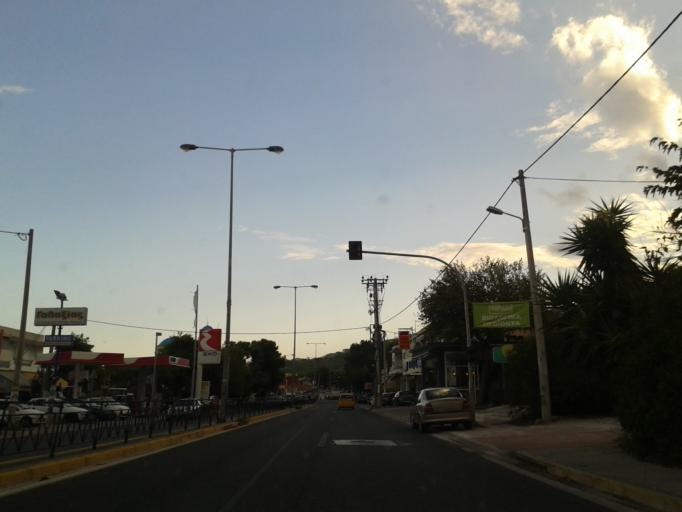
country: GR
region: Attica
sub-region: Nomarchia Anatolikis Attikis
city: Neos Voutzas
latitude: 38.0634
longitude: 23.9818
